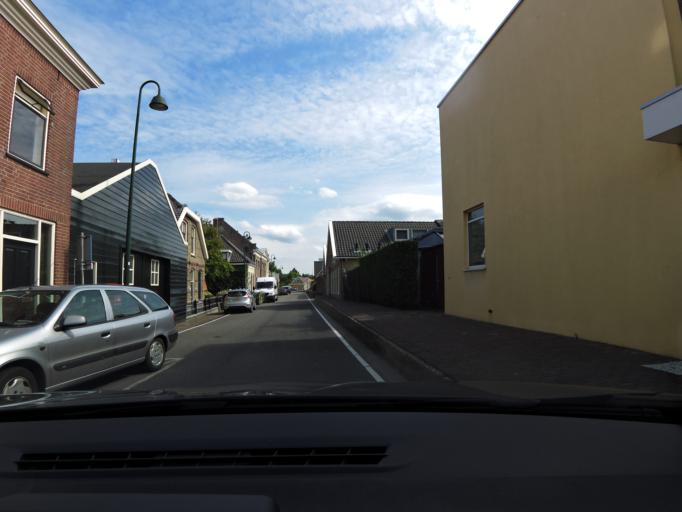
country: NL
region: South Holland
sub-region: Gemeente Schiedam
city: Schiedam
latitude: 51.9625
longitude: 4.3941
